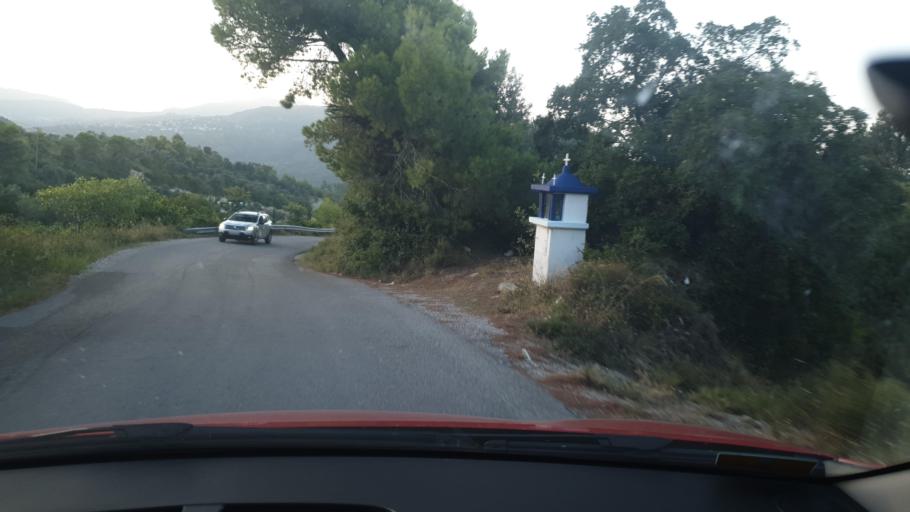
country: GR
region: Central Greece
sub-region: Nomos Evvoias
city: Oxilithos
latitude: 38.5949
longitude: 24.1177
